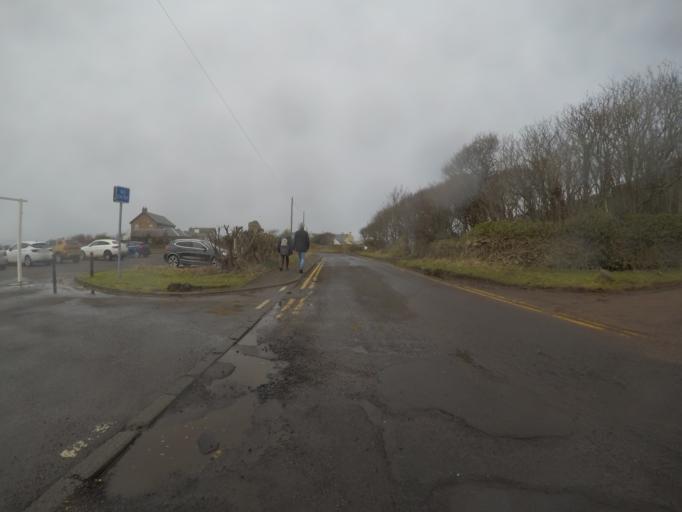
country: GB
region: Scotland
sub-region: North Ayrshire
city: West Kilbride
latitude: 55.6983
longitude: -4.9024
